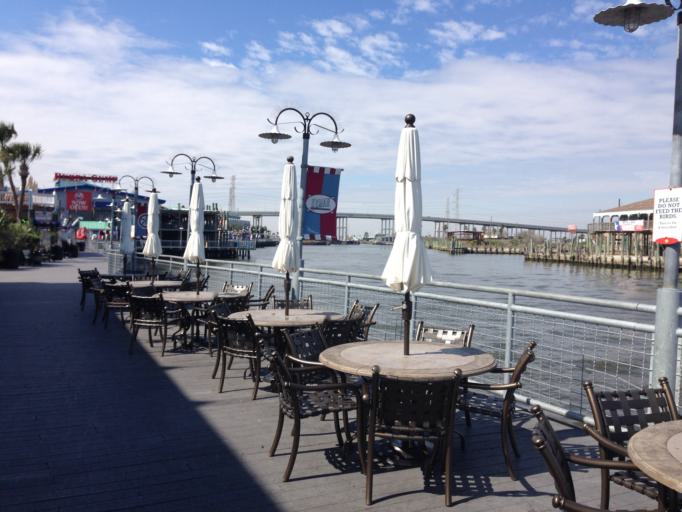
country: US
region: Texas
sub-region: Galveston County
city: Kemah
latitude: 29.5481
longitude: -95.0177
